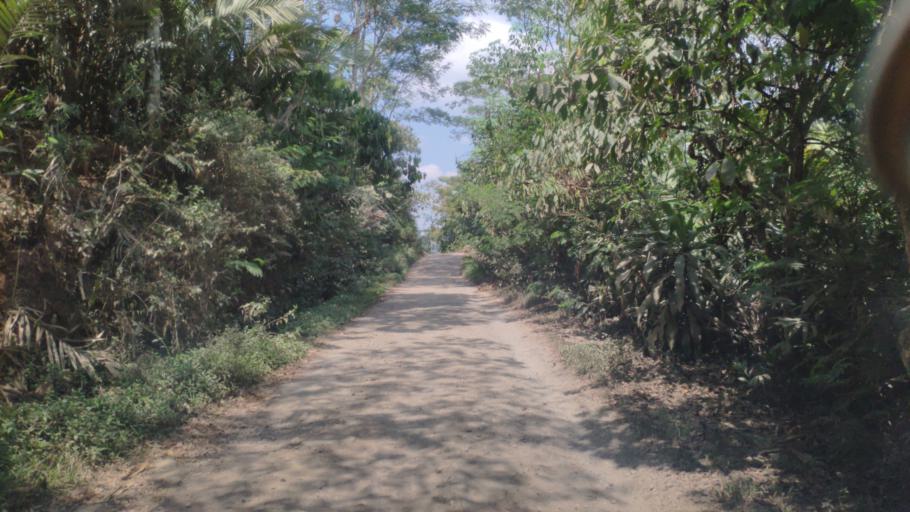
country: ID
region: Central Java
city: Wonosobo
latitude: -7.3220
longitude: 109.6636
